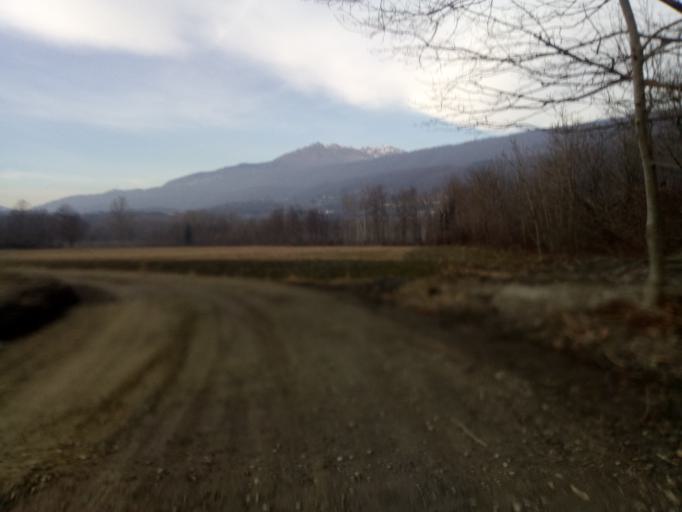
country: IT
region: Piedmont
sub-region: Provincia di Torino
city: Burolo
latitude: 45.4824
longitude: 7.9235
